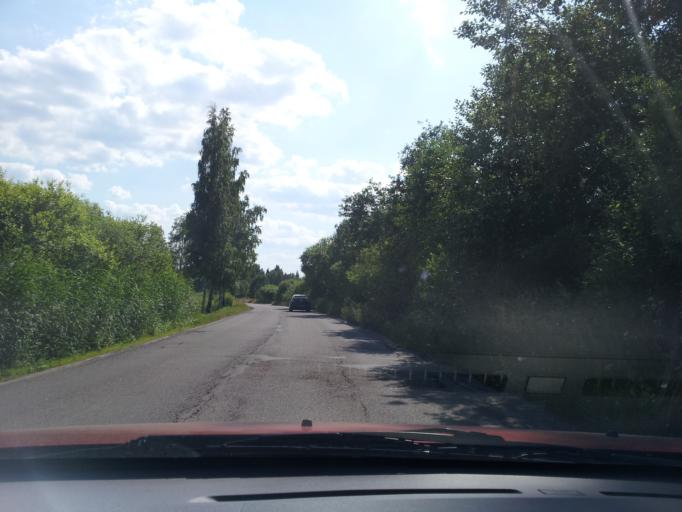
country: LV
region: Riga
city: Bolderaja
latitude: 57.0649
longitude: 24.0844
